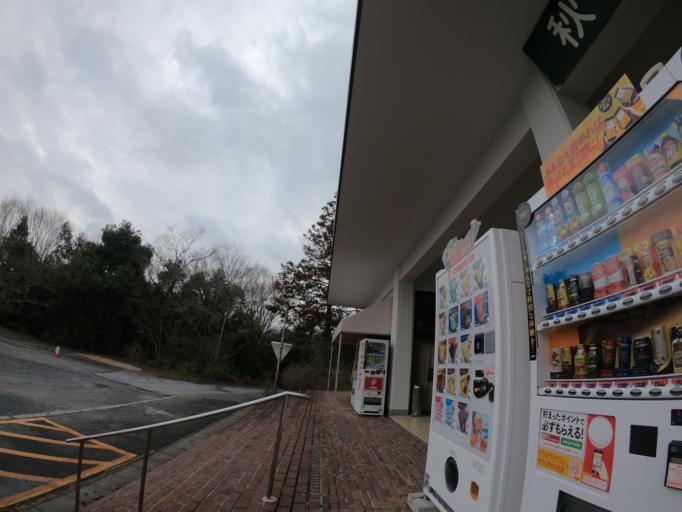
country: JP
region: Yamaguchi
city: Ogori-shimogo
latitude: 34.2320
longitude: 131.3040
